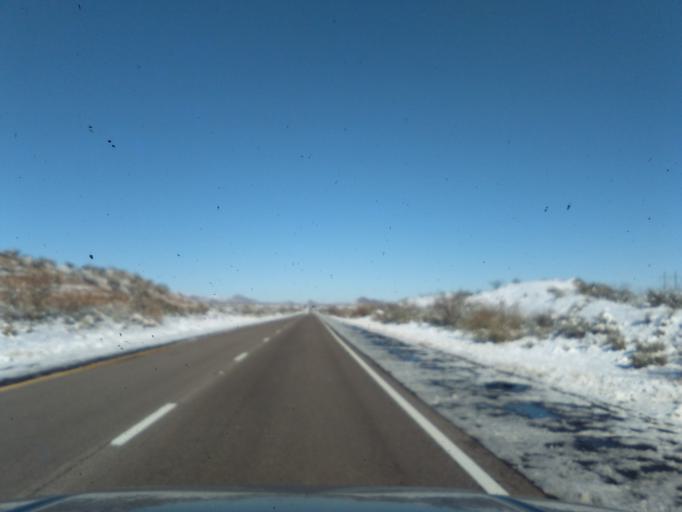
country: US
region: New Mexico
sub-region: Socorro County
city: Socorro
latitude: 33.6900
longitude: -107.0607
